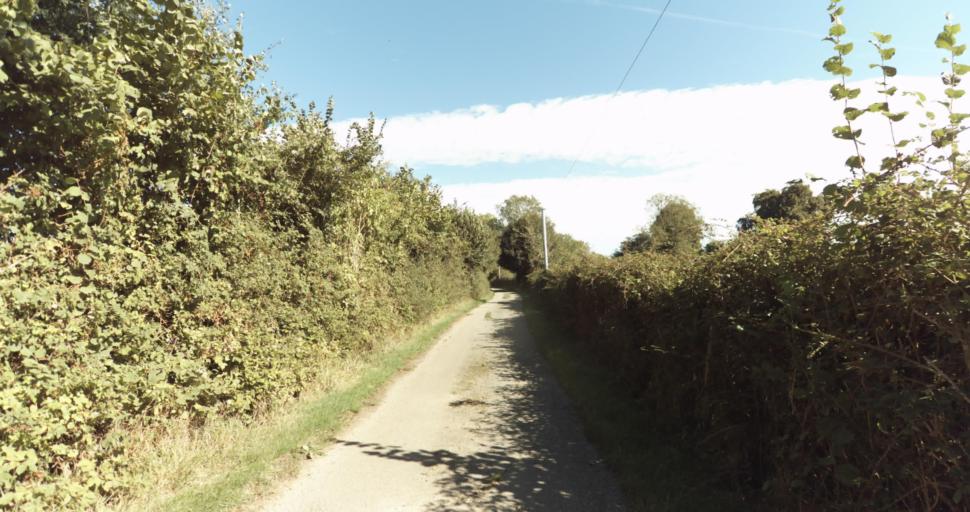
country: FR
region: Lower Normandy
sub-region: Departement de l'Orne
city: Gace
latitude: 48.7988
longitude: 0.2202
